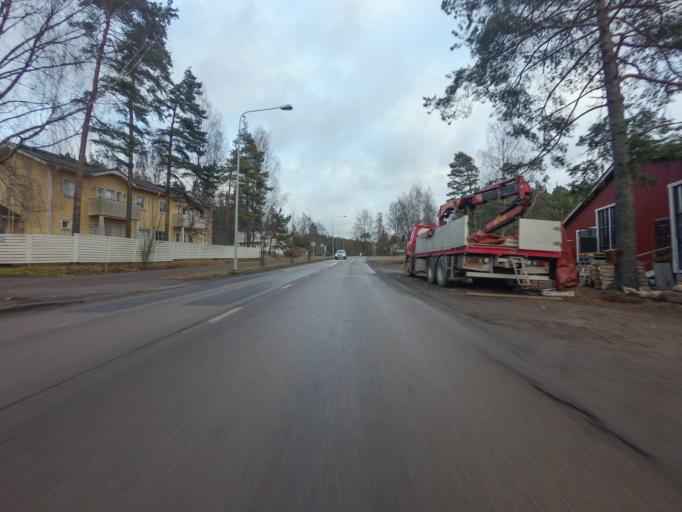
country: FI
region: Uusimaa
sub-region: Helsinki
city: Lohja
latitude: 60.2679
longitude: 24.1225
